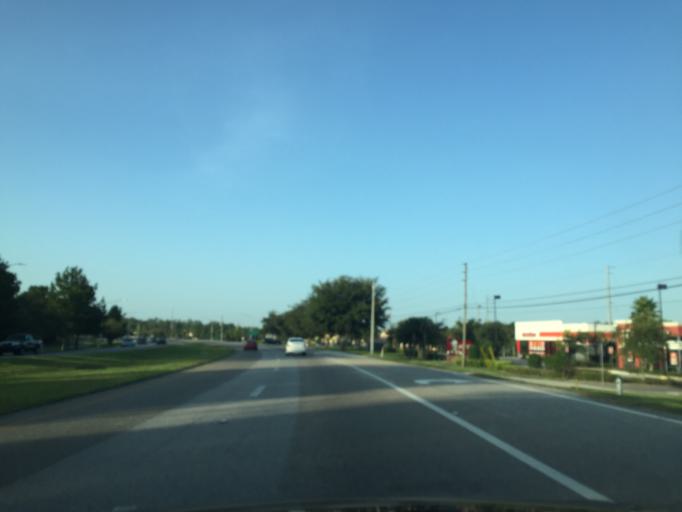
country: US
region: Florida
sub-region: Orange County
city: Alafaya
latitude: 28.5393
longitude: -81.2077
